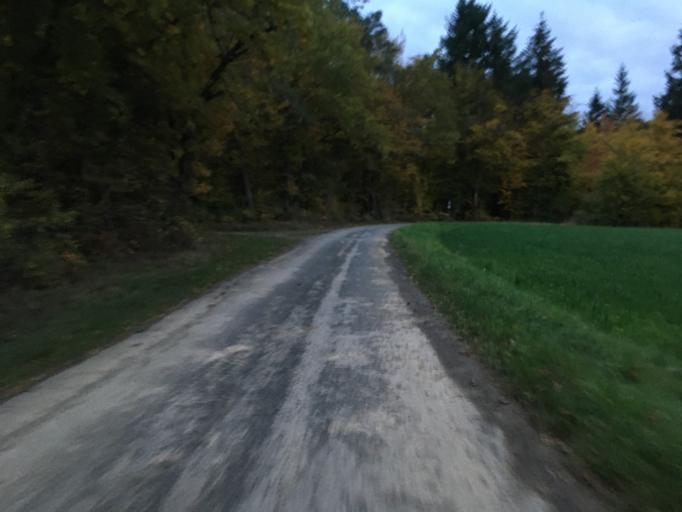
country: DE
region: Baden-Wuerttemberg
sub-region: Karlsruhe Region
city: Osterburken
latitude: 49.4503
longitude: 9.4312
